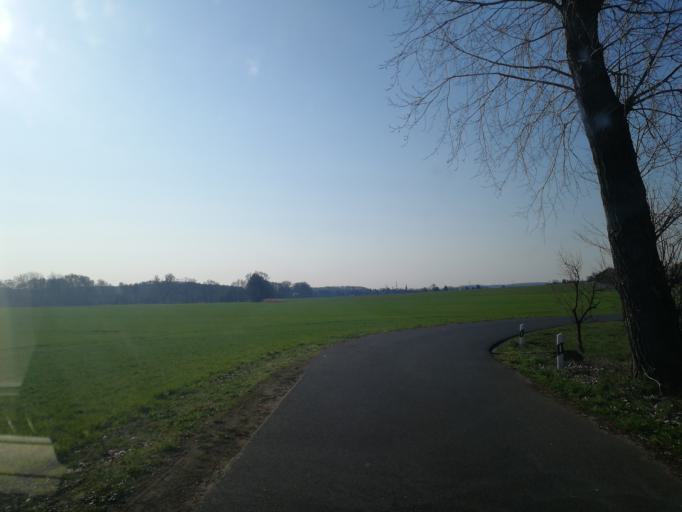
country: DE
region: Brandenburg
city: Drahnsdorf
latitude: 51.8849
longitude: 13.5839
